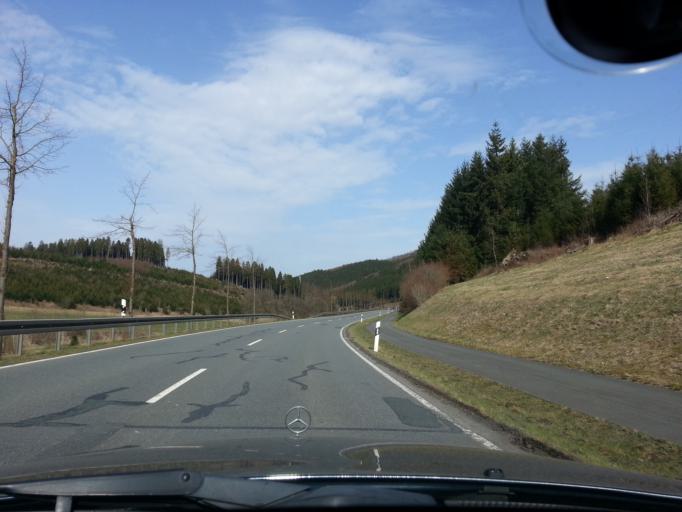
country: DE
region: North Rhine-Westphalia
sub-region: Regierungsbezirk Arnsberg
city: Bad Fredeburg
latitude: 51.2690
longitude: 8.3547
